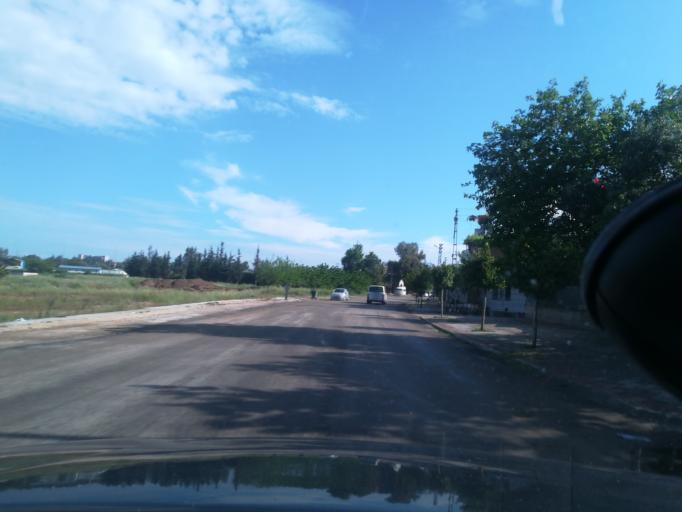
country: TR
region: Adana
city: Adana
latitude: 37.0215
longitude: 35.3629
